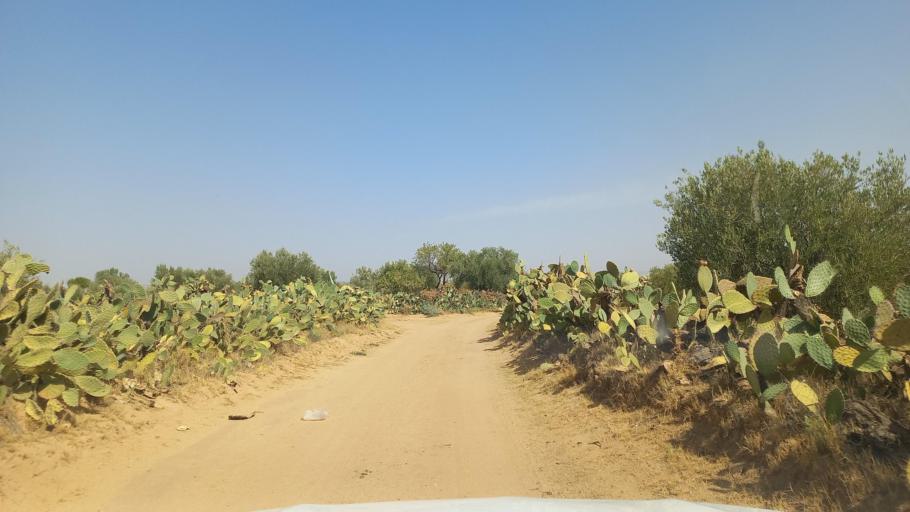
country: TN
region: Al Qasrayn
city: Kasserine
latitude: 35.2421
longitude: 9.0486
